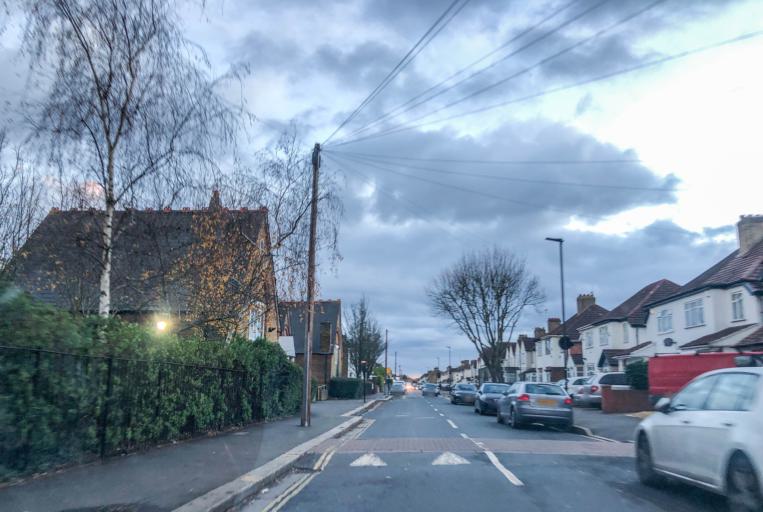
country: GB
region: England
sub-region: Greater London
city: Hounslow
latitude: 51.4648
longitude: -0.3736
